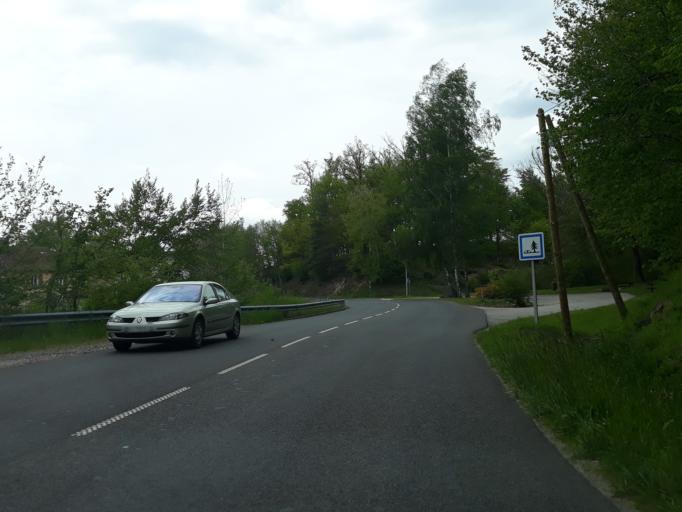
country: FR
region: Lorraine
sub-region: Departement des Vosges
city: Bruyeres
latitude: 48.1863
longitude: 6.7457
